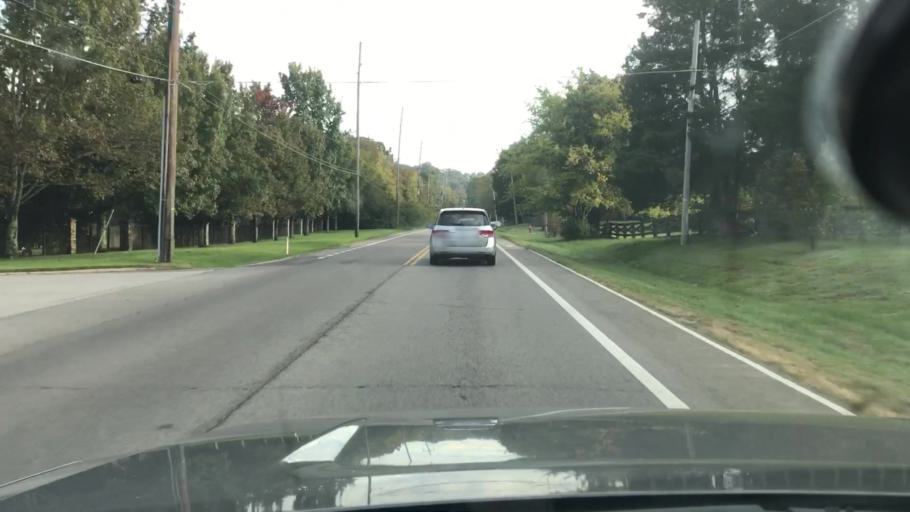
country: US
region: Tennessee
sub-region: Davidson County
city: Forest Hills
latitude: 36.0719
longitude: -86.8415
